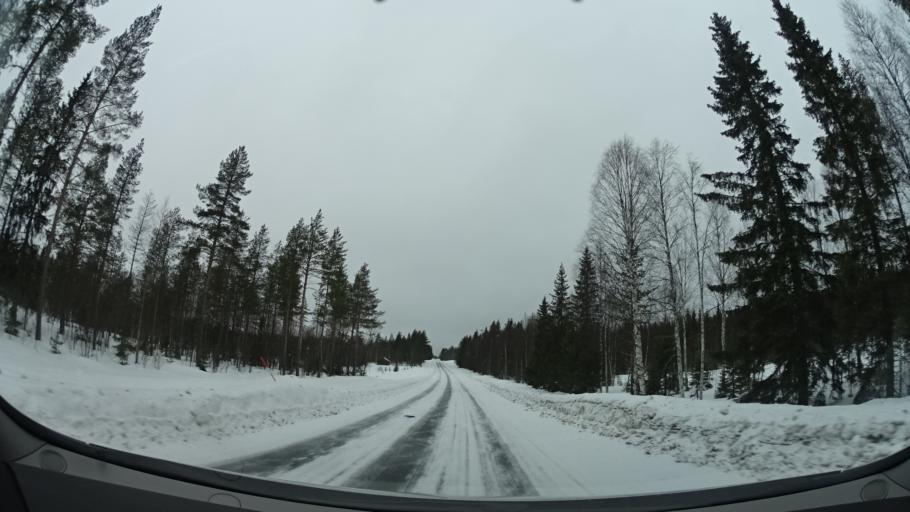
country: SE
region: Vaesterbotten
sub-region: Mala Kommun
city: Mala
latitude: 65.0916
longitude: 18.9460
